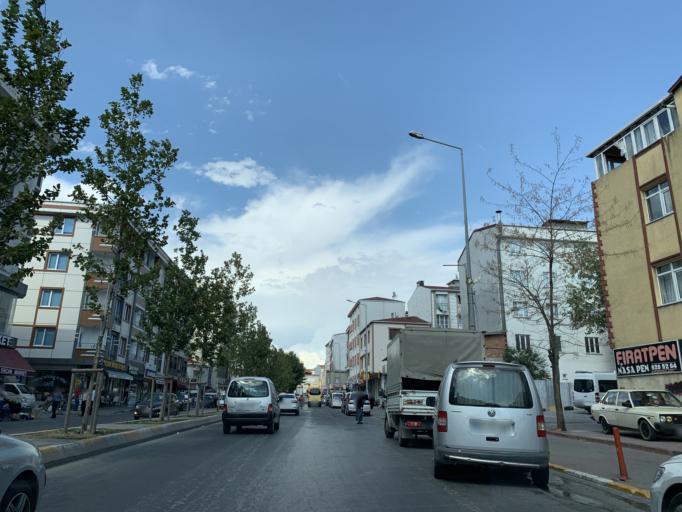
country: TR
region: Istanbul
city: Esenyurt
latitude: 41.0443
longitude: 28.6645
